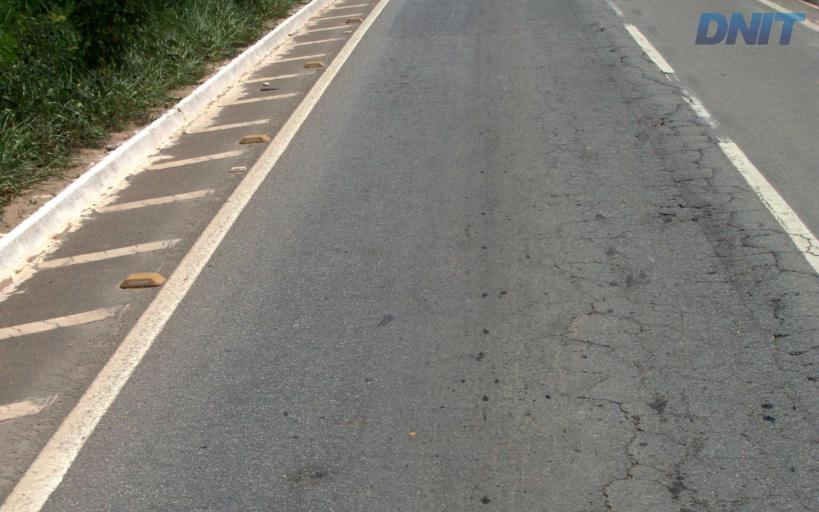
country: BR
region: Minas Gerais
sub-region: Governador Valadares
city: Governador Valadares
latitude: -18.8892
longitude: -42.0049
